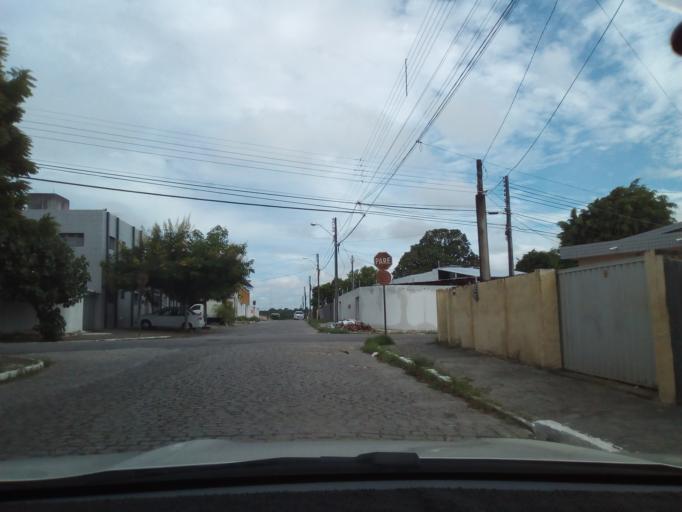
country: BR
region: Paraiba
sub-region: Joao Pessoa
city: Joao Pessoa
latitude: -7.1255
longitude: -34.8560
